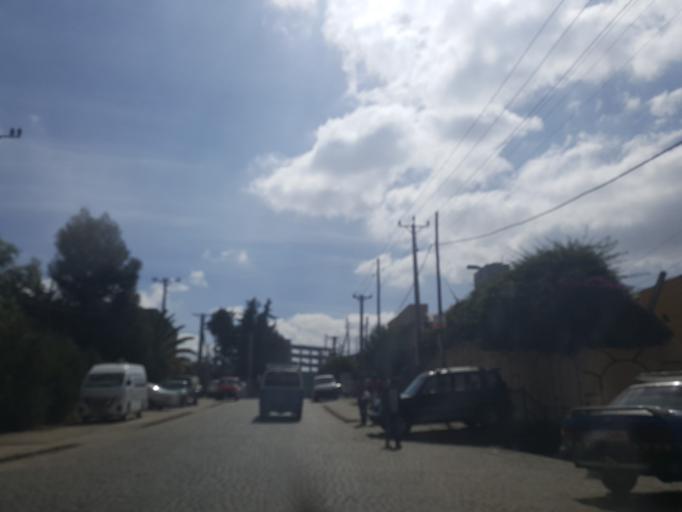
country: ET
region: Adis Abeba
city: Addis Ababa
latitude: 9.0511
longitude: 38.7270
